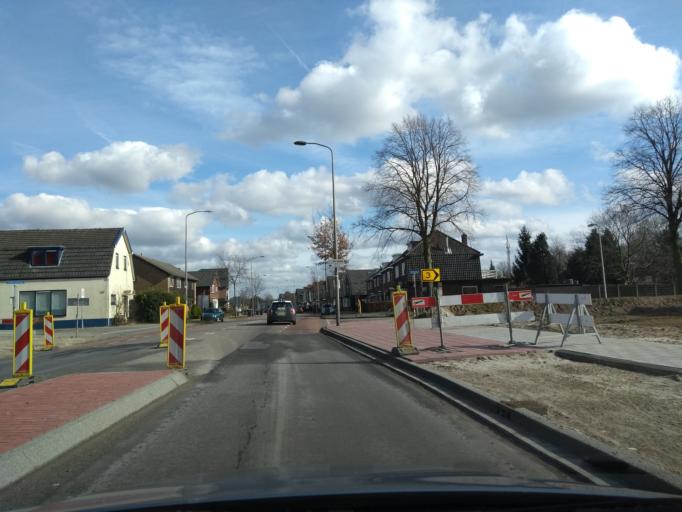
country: NL
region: Overijssel
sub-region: Gemeente Hengelo
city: Hengelo
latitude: 52.2516
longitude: 6.7907
